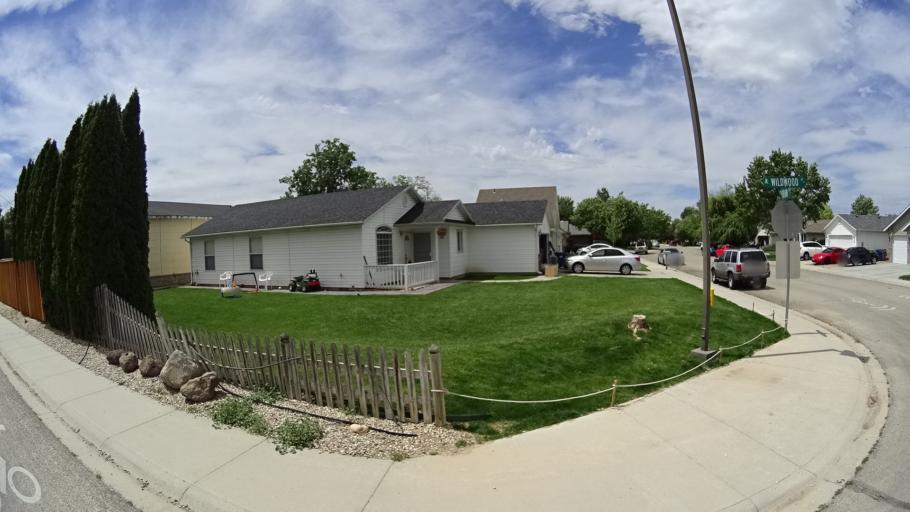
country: US
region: Idaho
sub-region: Ada County
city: Meridian
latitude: 43.6288
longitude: -116.3219
